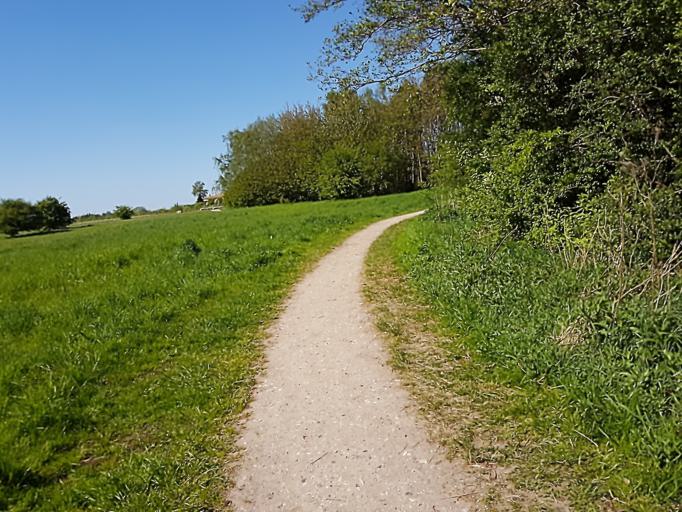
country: DK
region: Capital Region
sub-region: Egedal Kommune
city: Olstykke
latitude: 55.7915
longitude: 12.1380
